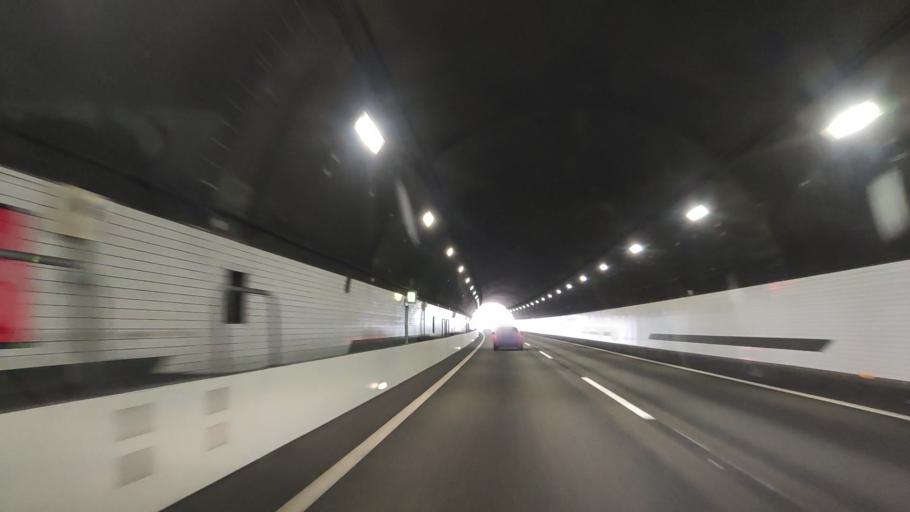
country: JP
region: Tokushima
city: Ishii
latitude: 34.1966
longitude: 134.4321
